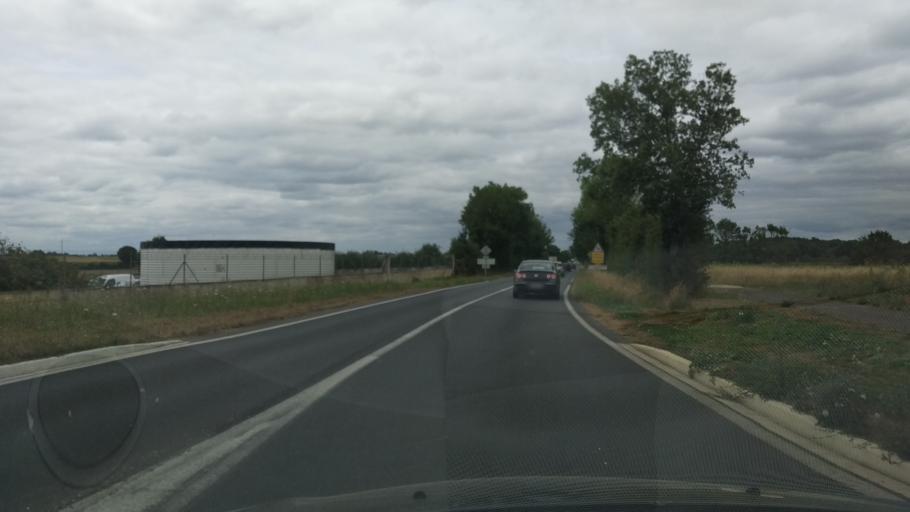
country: FR
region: Poitou-Charentes
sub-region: Departement de la Vienne
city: Roches-Premarie-Andille
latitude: 46.4950
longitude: 0.3659
